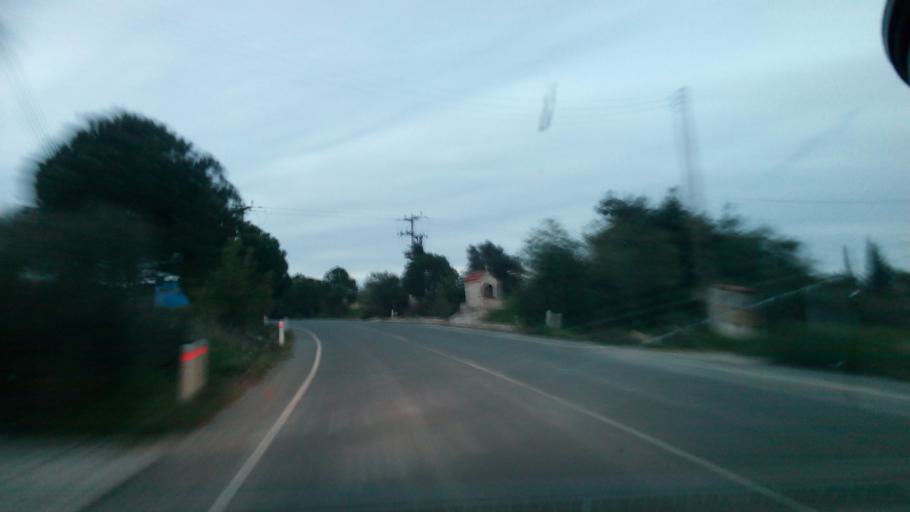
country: CY
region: Pafos
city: Polis
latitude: 34.9856
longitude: 32.4977
